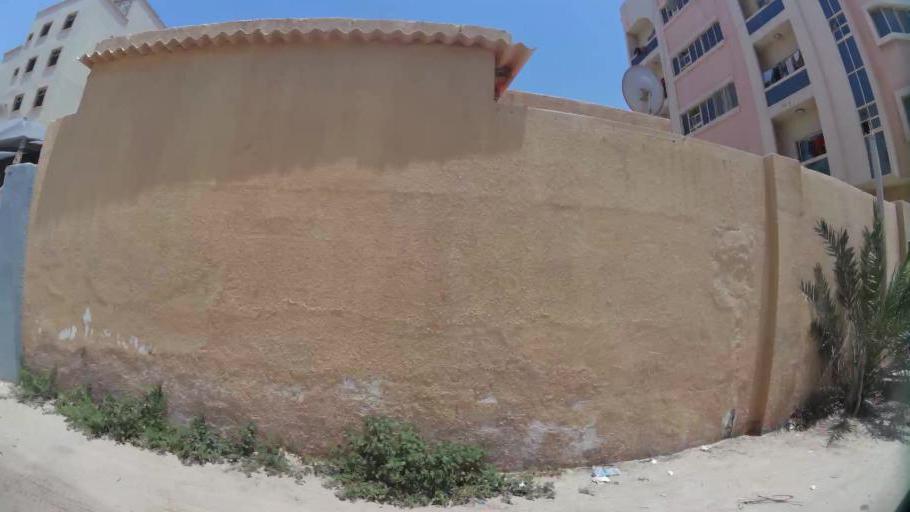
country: AE
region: Ajman
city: Ajman
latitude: 25.4063
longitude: 55.4359
